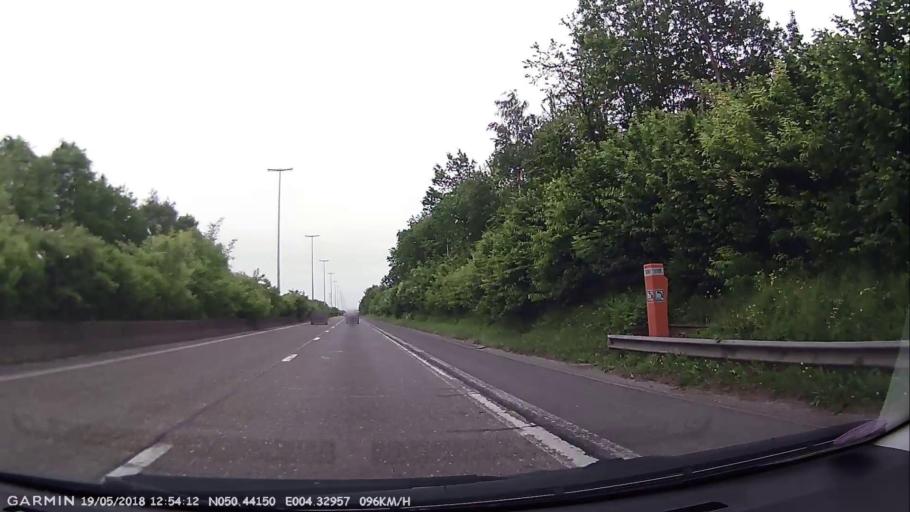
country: BE
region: Wallonia
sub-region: Province du Hainaut
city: Courcelles
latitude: 50.4418
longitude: 4.3292
